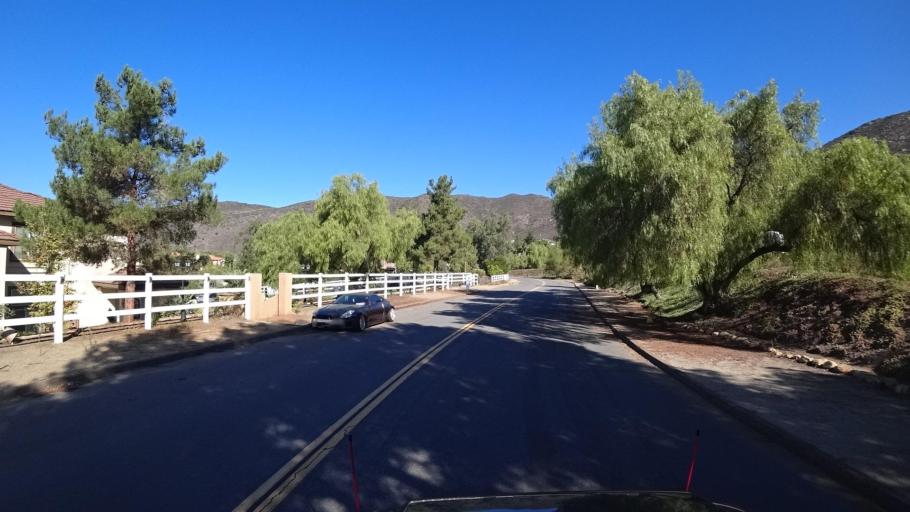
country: US
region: California
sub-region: San Diego County
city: Jamul
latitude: 32.7399
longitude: -116.8551
